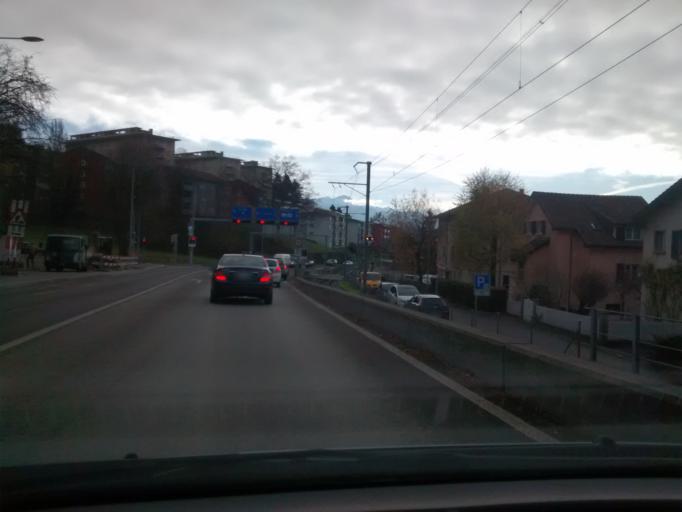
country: CH
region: Vaud
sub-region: Ouest Lausannois District
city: Prilly
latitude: 46.5410
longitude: 6.6067
